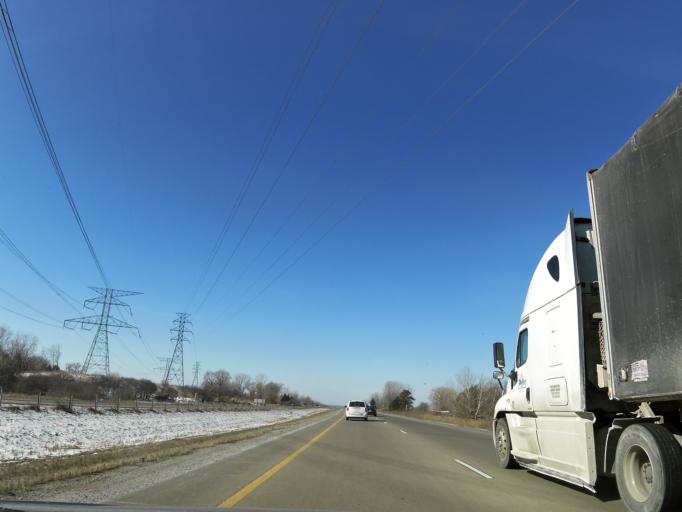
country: US
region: Minnesota
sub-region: Ramsey County
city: North Saint Paul
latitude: 45.0351
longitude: -92.9903
